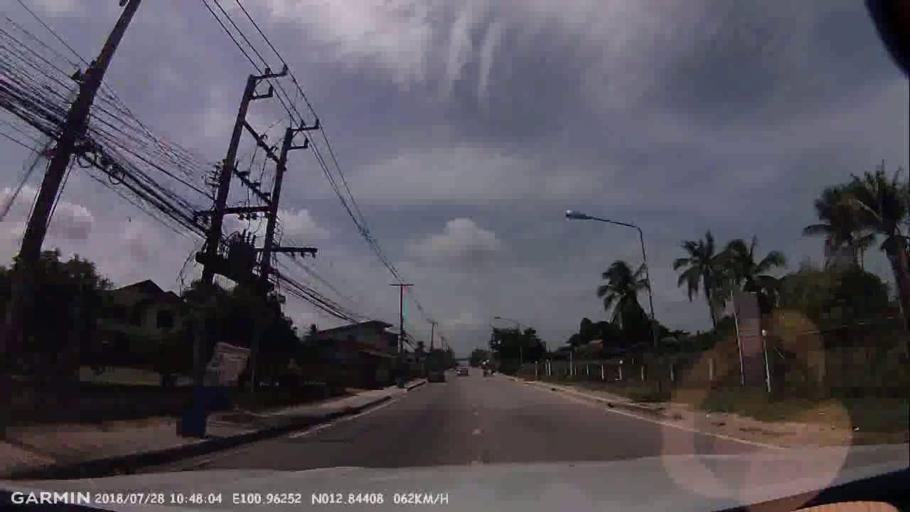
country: TH
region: Chon Buri
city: Phatthaya
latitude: 12.8440
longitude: 100.9626
